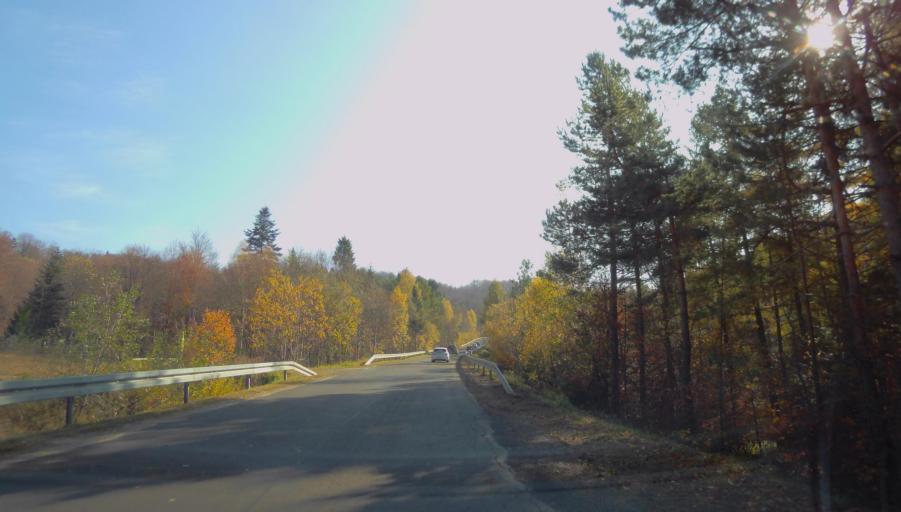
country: PL
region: Subcarpathian Voivodeship
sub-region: Powiat leski
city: Cisna
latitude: 49.2163
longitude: 22.2336
